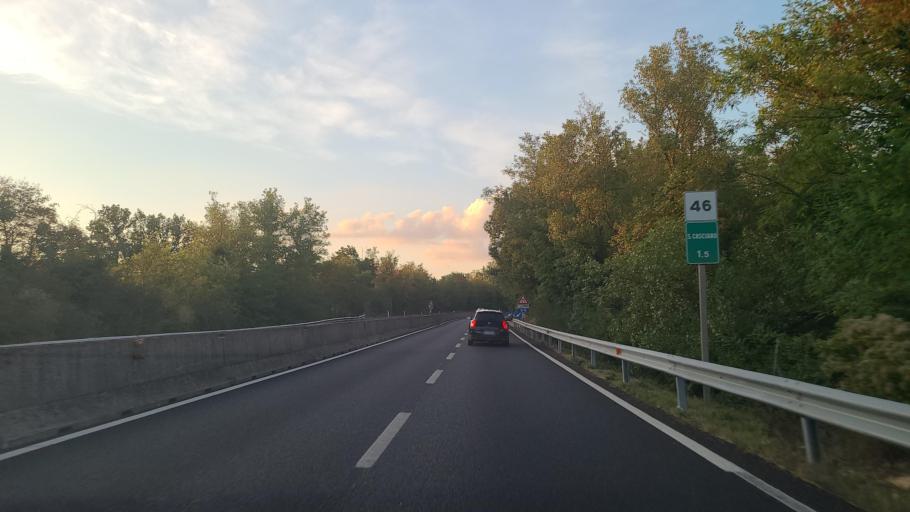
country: IT
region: Tuscany
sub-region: Province of Florence
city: San Casciano in Val di Pesa
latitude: 43.6405
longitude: 11.1787
